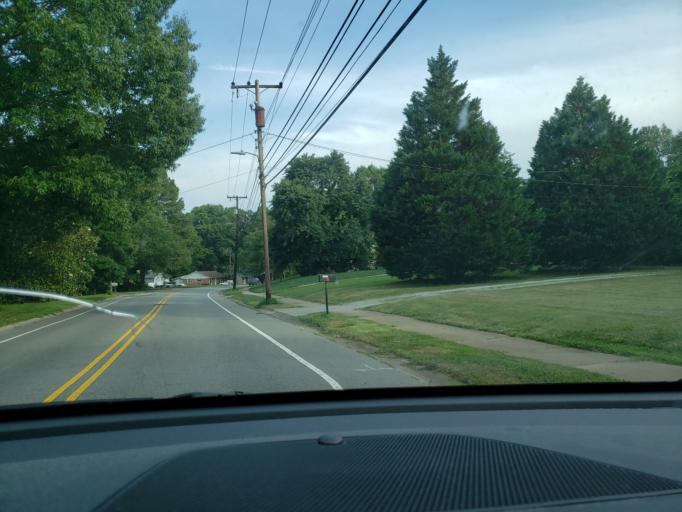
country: US
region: North Carolina
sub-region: Durham County
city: Durham
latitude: 35.8999
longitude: -78.9111
